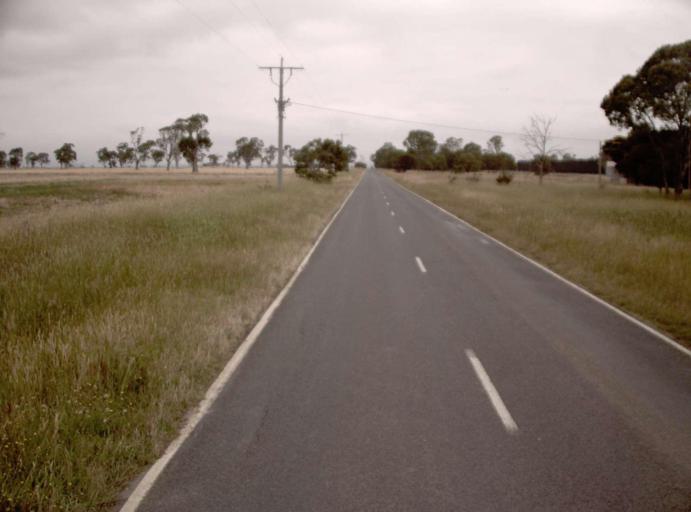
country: AU
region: Victoria
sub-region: Wellington
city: Heyfield
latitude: -38.0540
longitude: 146.7685
